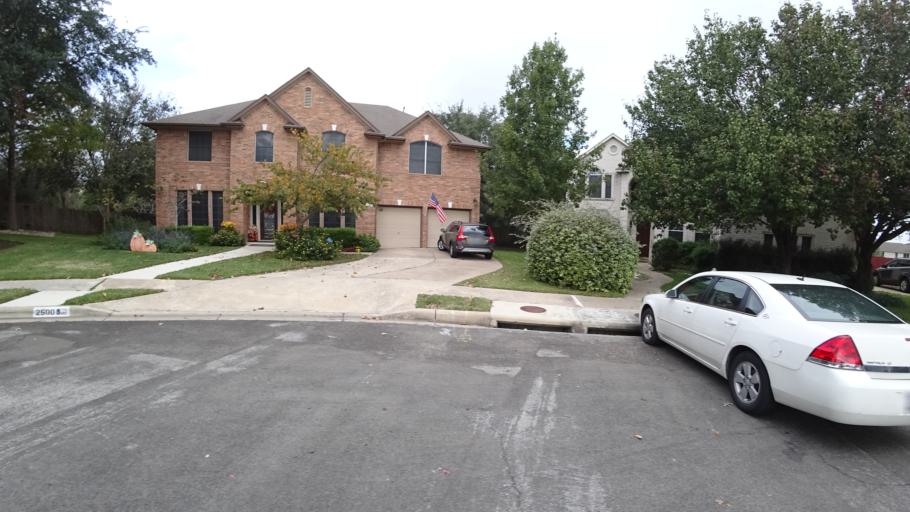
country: US
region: Texas
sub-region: Travis County
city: Shady Hollow
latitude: 30.1571
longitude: -97.8465
